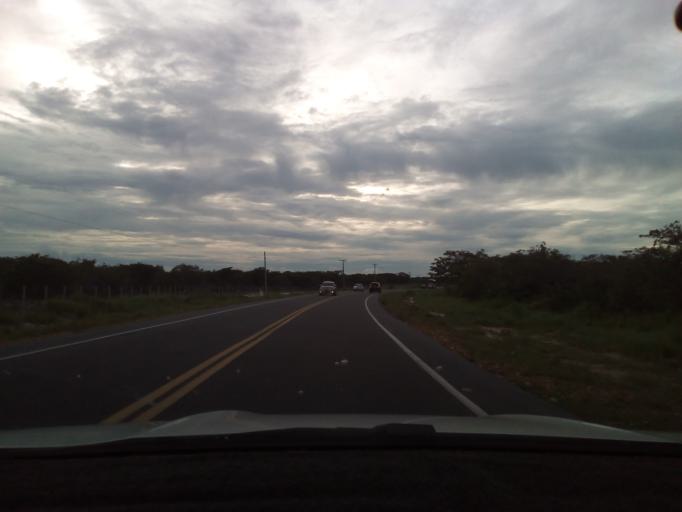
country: BR
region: Ceara
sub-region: Beberibe
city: Beberibe
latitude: -4.3655
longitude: -37.9521
